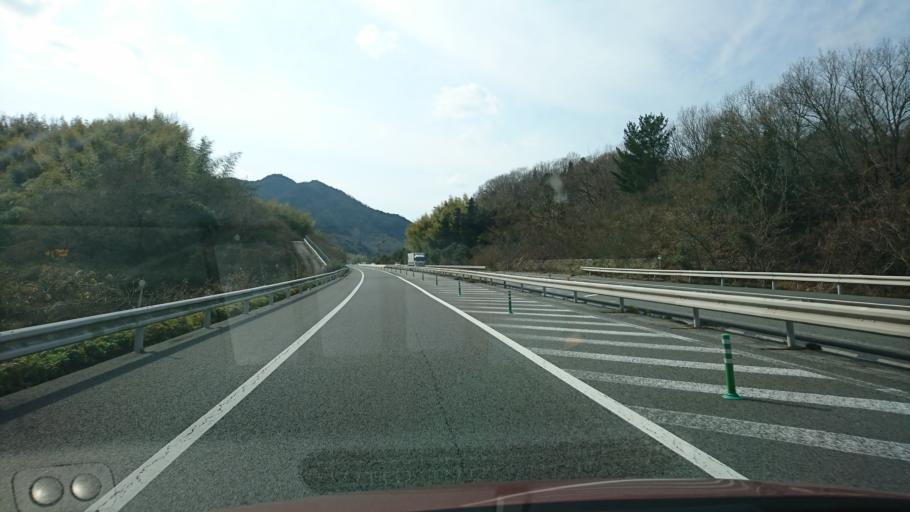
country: JP
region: Hiroshima
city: Innoshima
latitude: 34.1394
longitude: 133.0551
